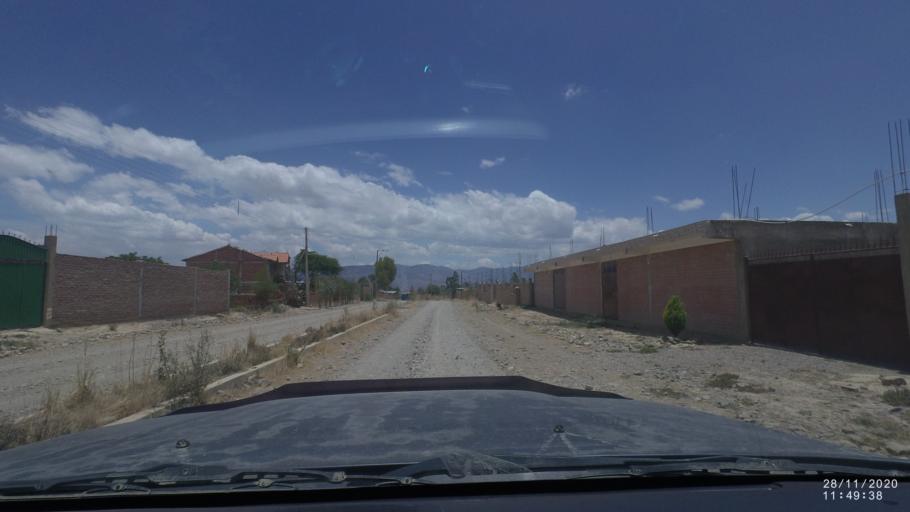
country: BO
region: Cochabamba
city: Tarata
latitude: -17.6297
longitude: -66.0282
